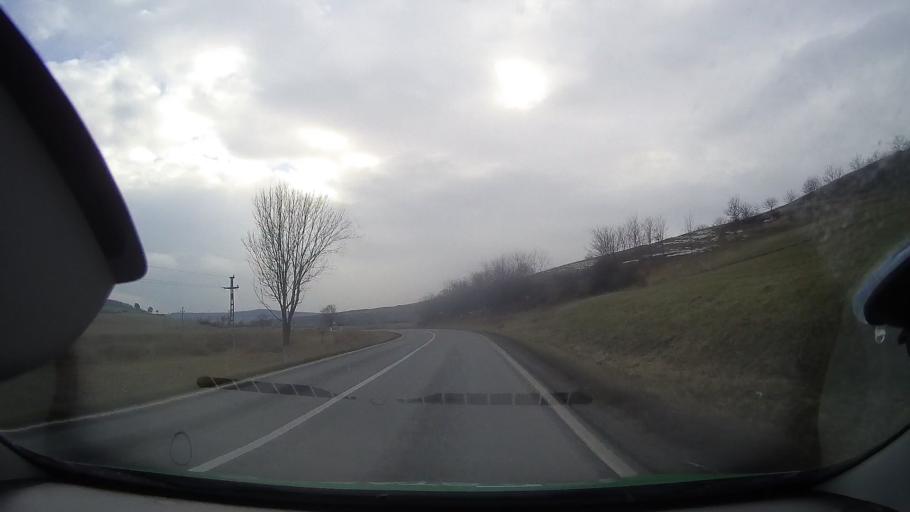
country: RO
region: Mures
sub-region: Comuna Cucerdea
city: Cucerdea
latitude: 46.3847
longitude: 24.2546
